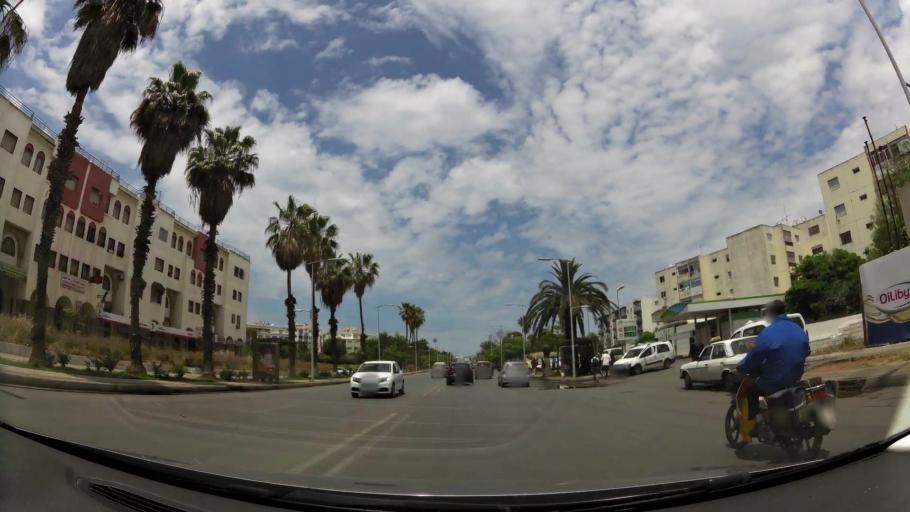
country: MA
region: Rabat-Sale-Zemmour-Zaer
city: Sale
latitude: 34.0409
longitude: -6.8162
